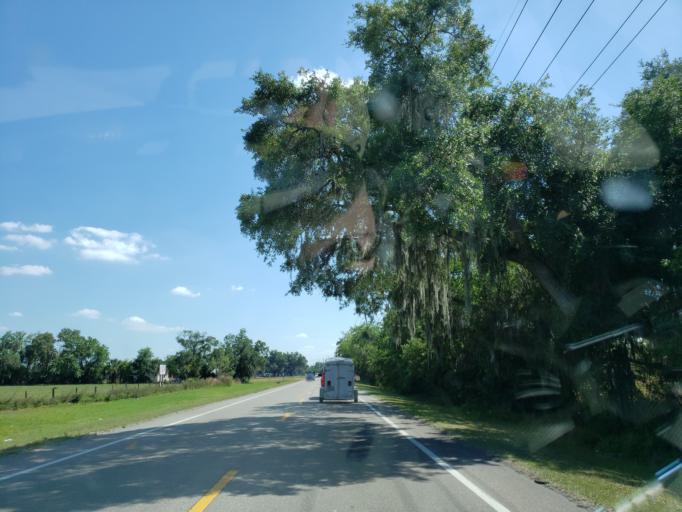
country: US
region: Florida
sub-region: Hillsborough County
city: Fish Hawk
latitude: 27.9026
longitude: -82.1273
